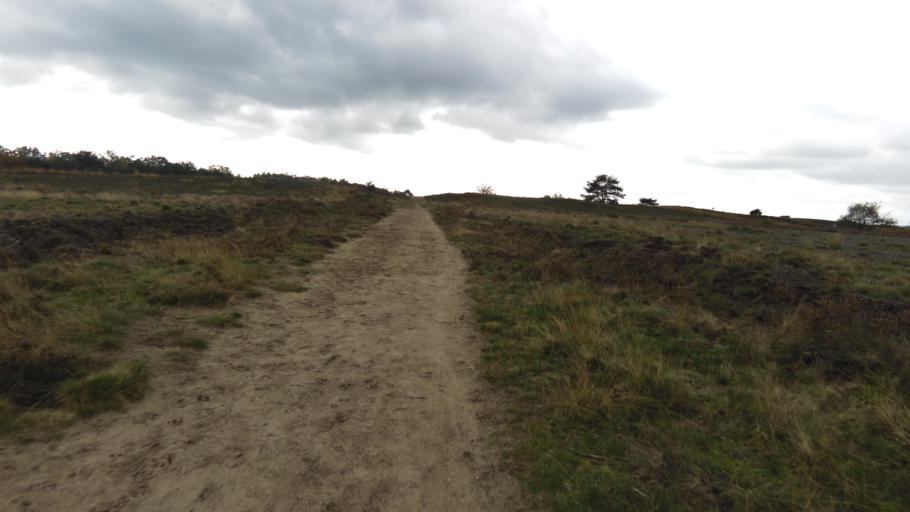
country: NL
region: Gelderland
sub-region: Gemeente Nunspeet
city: Nunspeet
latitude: 52.3293
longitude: 5.8153
